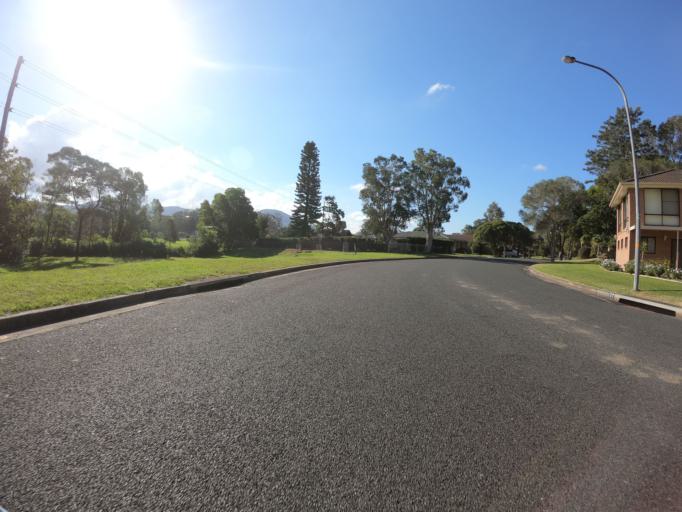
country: AU
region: New South Wales
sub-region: Wollongong
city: Cordeaux Heights
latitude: -34.4412
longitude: 150.8468
